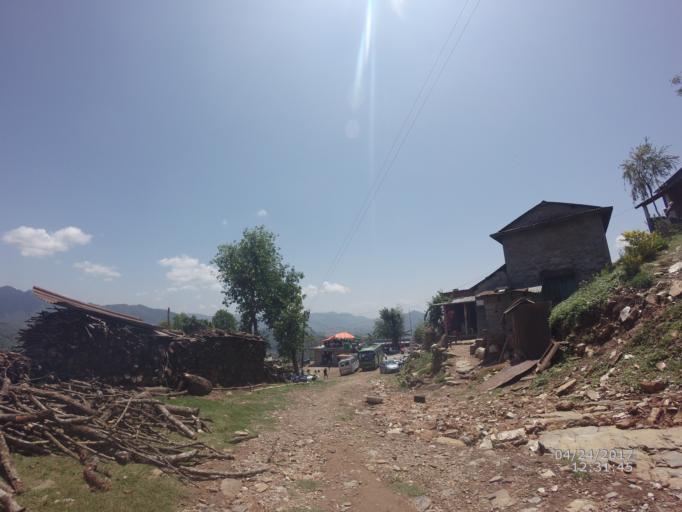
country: NP
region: Western Region
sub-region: Gandaki Zone
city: Pokhara
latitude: 28.1877
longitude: 84.0871
